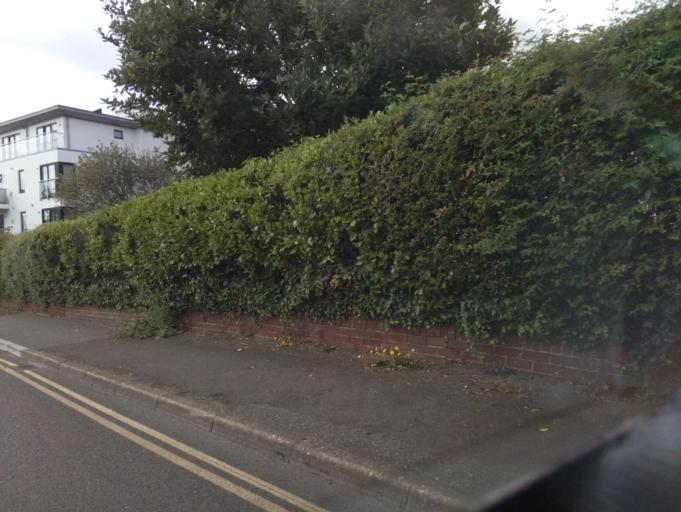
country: GB
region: England
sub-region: Poole
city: Poole
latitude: 50.7189
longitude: -1.9741
